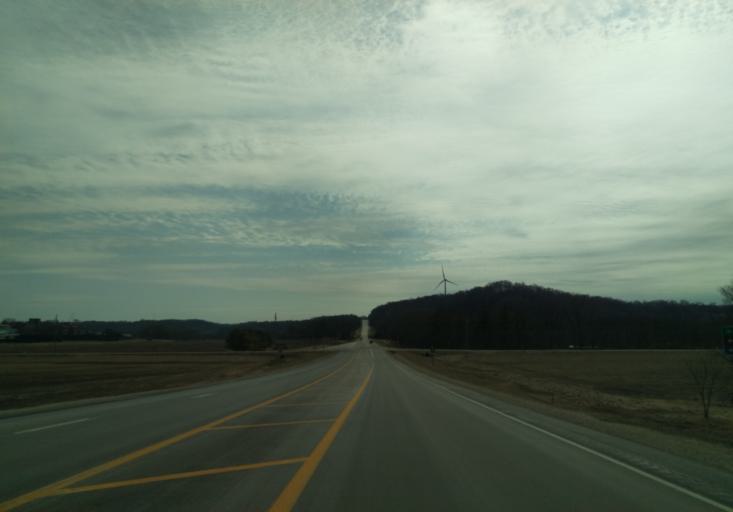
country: US
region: Iowa
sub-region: Winneshiek County
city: Decorah
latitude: 43.3227
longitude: -91.8137
